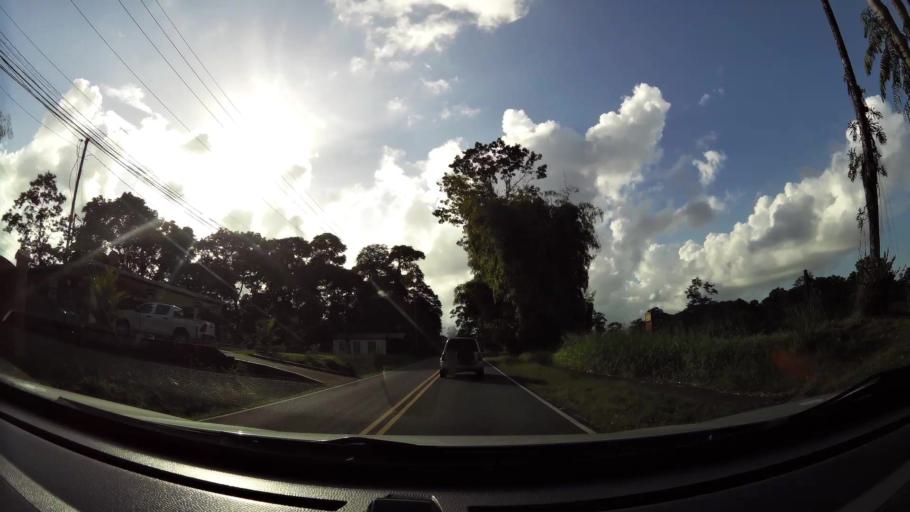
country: CR
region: Limon
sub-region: Canton de Siquirres
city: Siquirres
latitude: 10.0963
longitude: -83.5310
